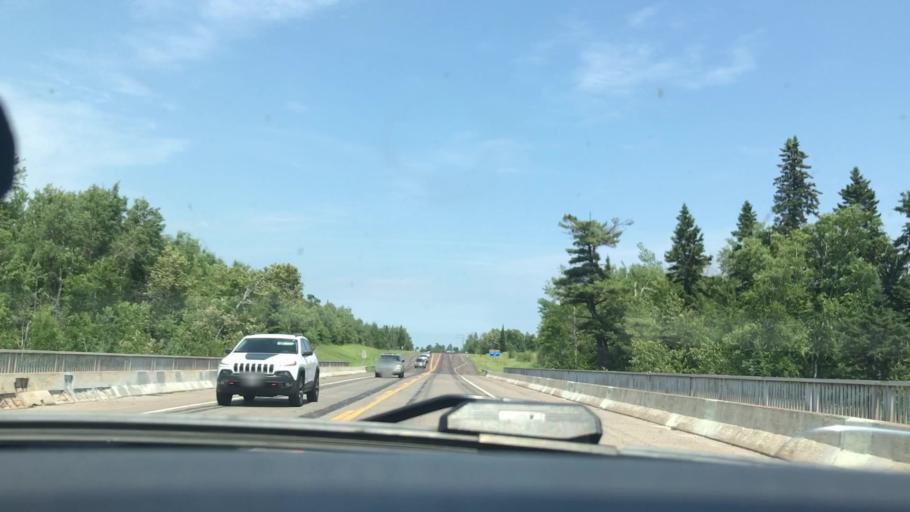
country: US
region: Minnesota
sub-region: Lake County
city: Silver Bay
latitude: 47.3375
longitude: -91.2004
